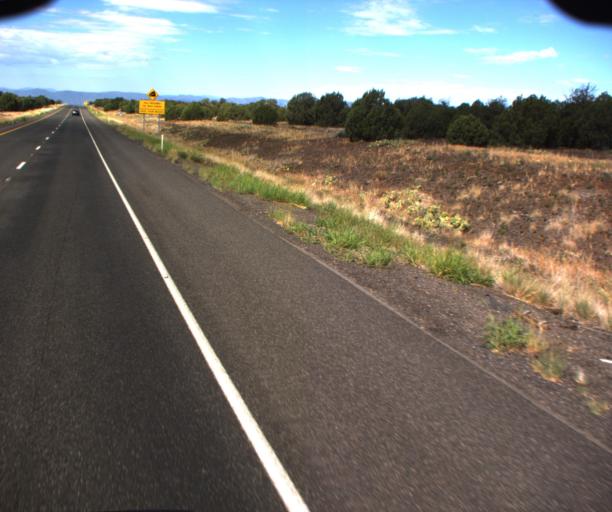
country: US
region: Arizona
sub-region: Yavapai County
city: Big Park
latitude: 34.7362
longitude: -111.6977
